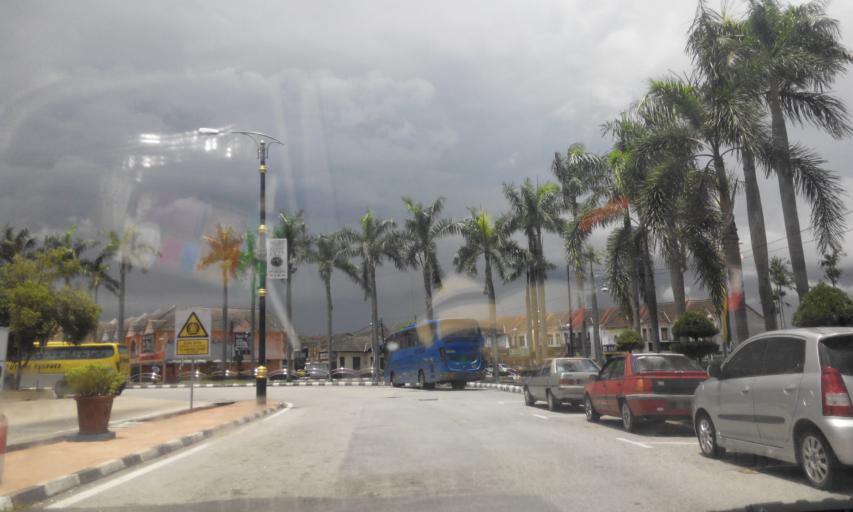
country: MY
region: Perak
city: Parit Buntar
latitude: 5.1182
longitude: 100.4874
